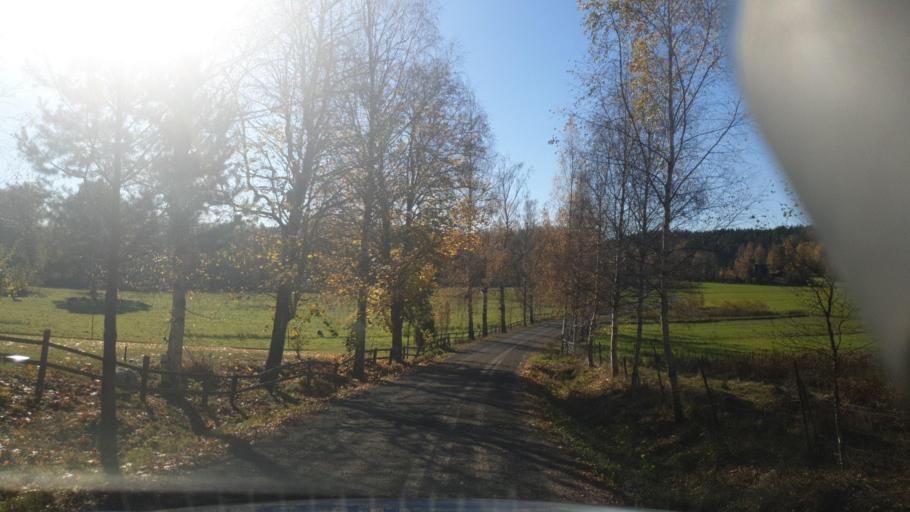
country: SE
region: Vaermland
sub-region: Grums Kommun
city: Grums
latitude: 59.4846
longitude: 12.9344
